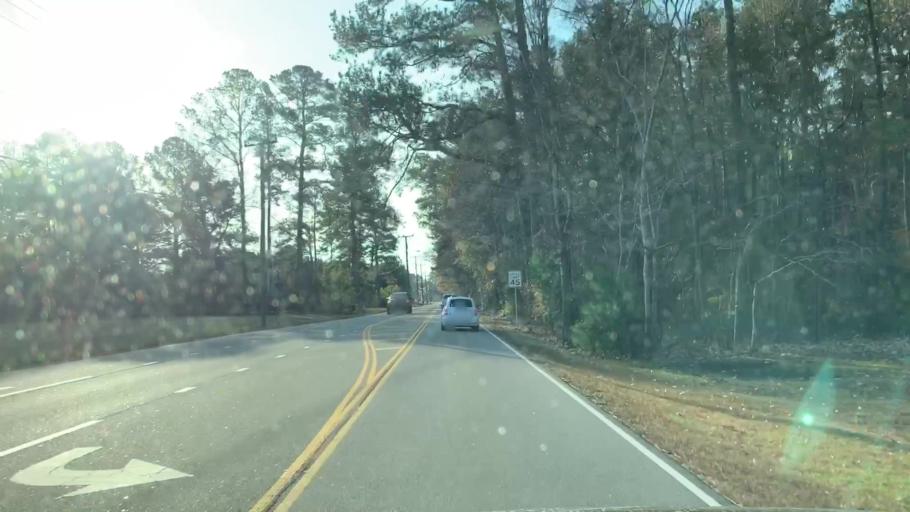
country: US
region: Virginia
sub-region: City of Chesapeake
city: Chesapeake
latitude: 36.7759
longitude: -76.1561
